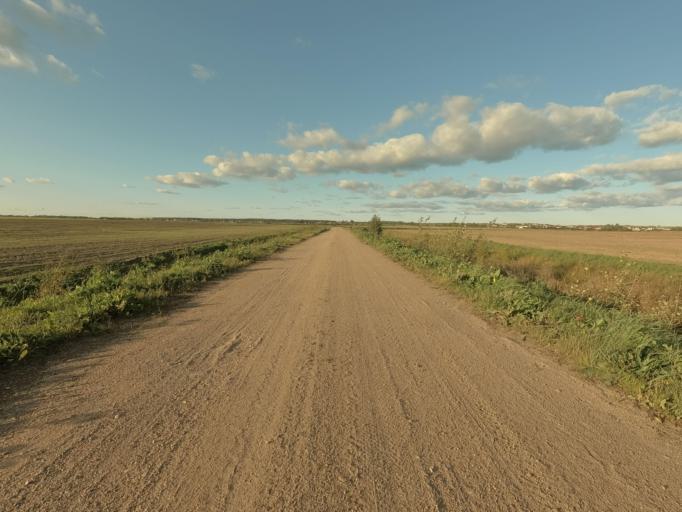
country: RU
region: Leningrad
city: Otradnoye
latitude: 59.8628
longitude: 30.7541
